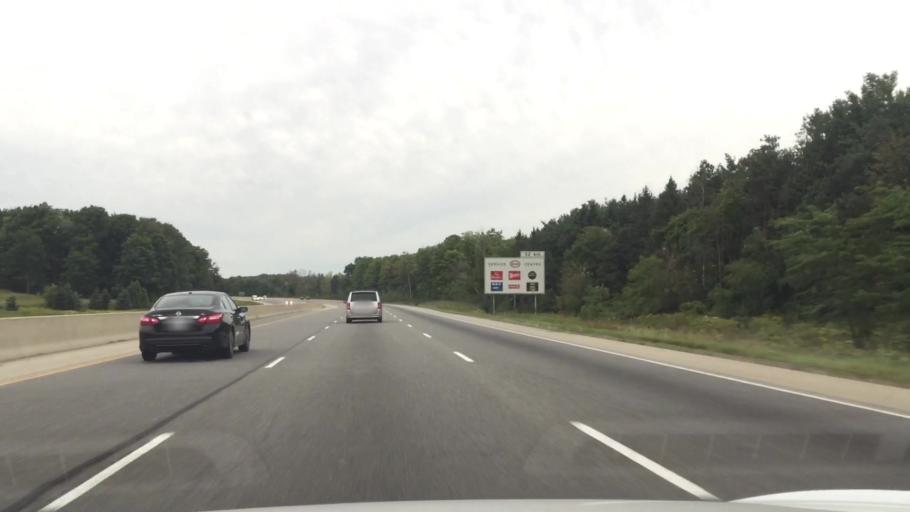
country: CA
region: Ontario
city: Kitchener
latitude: 43.2689
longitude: -80.5474
